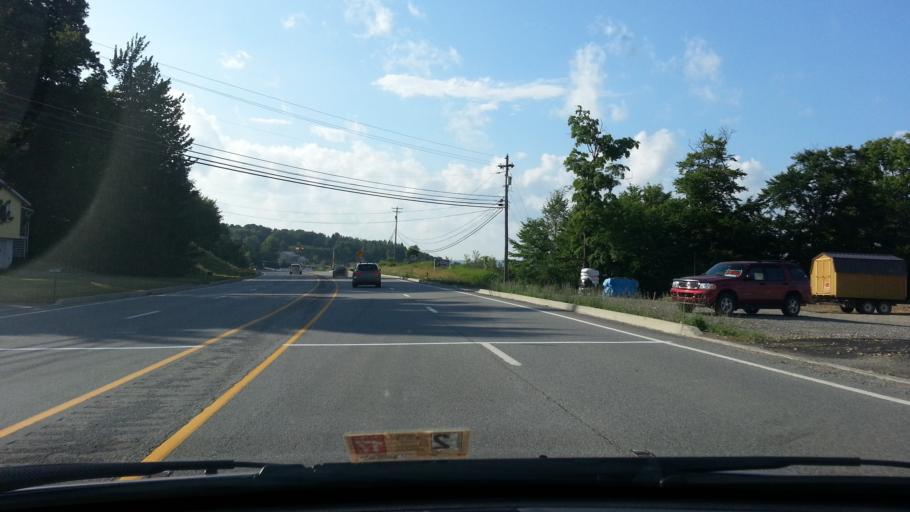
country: US
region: Pennsylvania
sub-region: Elk County
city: Saint Marys
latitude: 41.3978
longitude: -78.5574
